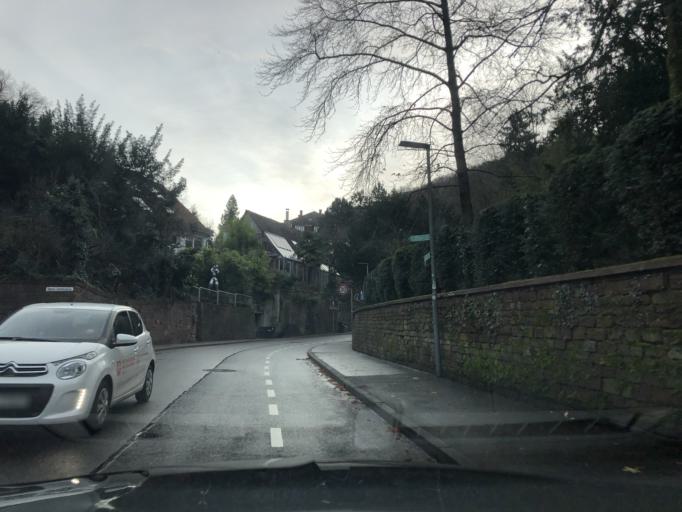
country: DE
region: Baden-Wuerttemberg
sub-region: Karlsruhe Region
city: Heidelberg
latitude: 49.3977
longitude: 8.6936
